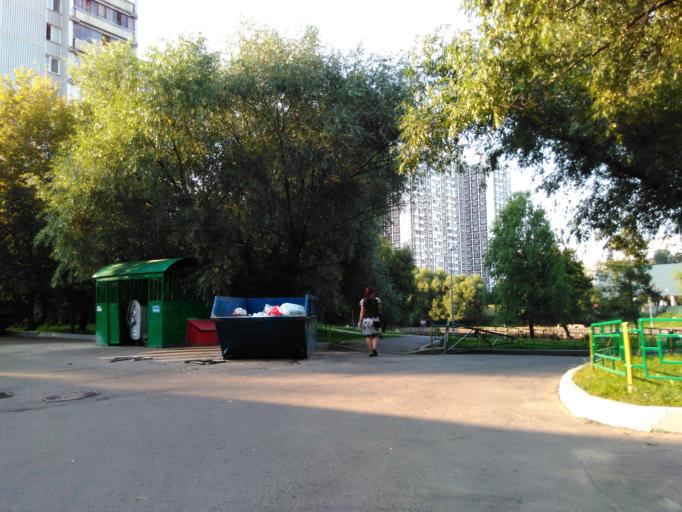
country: RU
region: Moscow
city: Yasenevo
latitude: 55.6357
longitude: 37.5296
